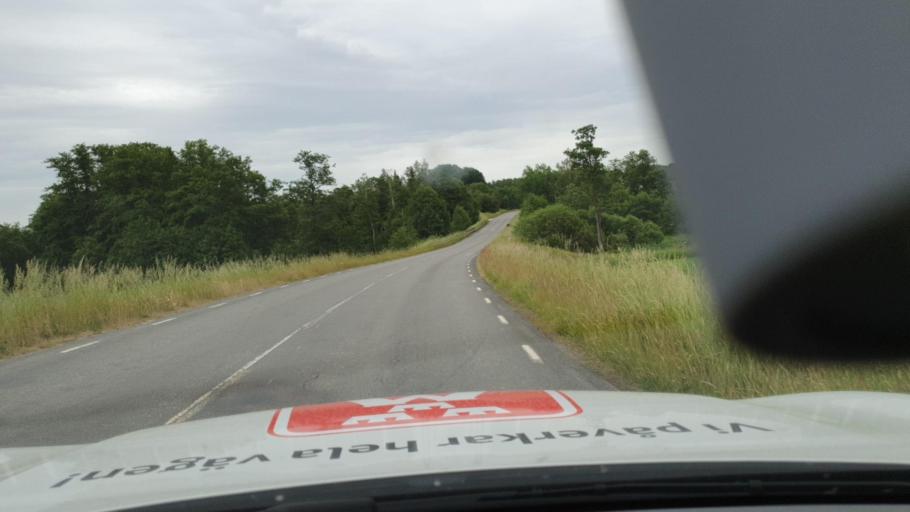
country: SE
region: Vaestra Goetaland
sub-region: Tidaholms Kommun
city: Olofstorp
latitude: 58.3036
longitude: 14.0855
